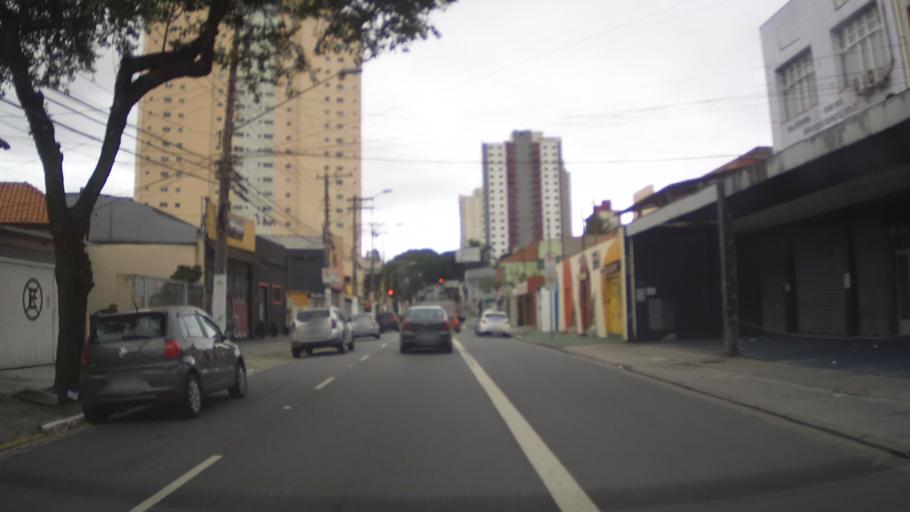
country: BR
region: Sao Paulo
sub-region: Guarulhos
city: Guarulhos
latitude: -23.5268
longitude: -46.5265
